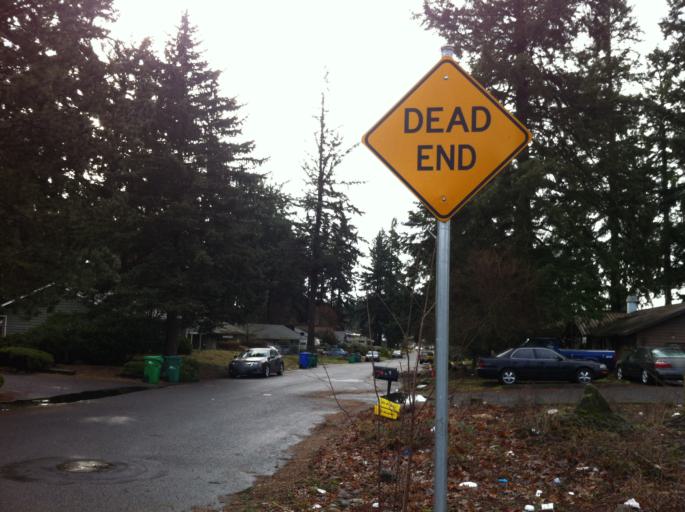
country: US
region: Oregon
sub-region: Multnomah County
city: Lents
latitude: 45.5190
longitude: -122.5240
